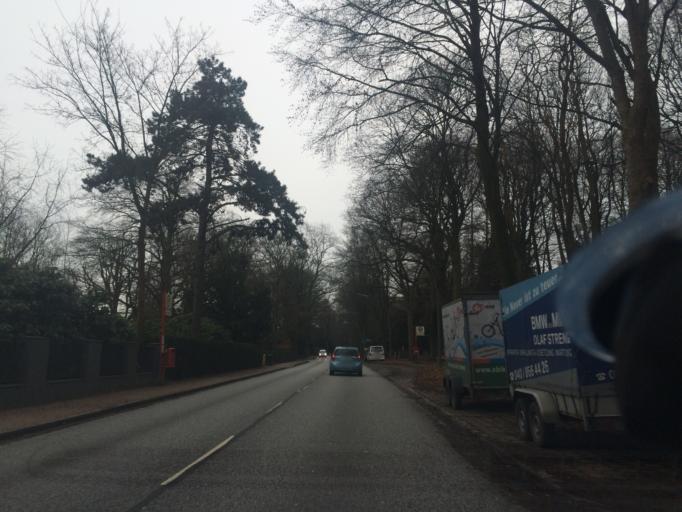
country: DE
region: Schleswig-Holstein
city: Halstenbek
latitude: 53.5555
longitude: 9.8345
